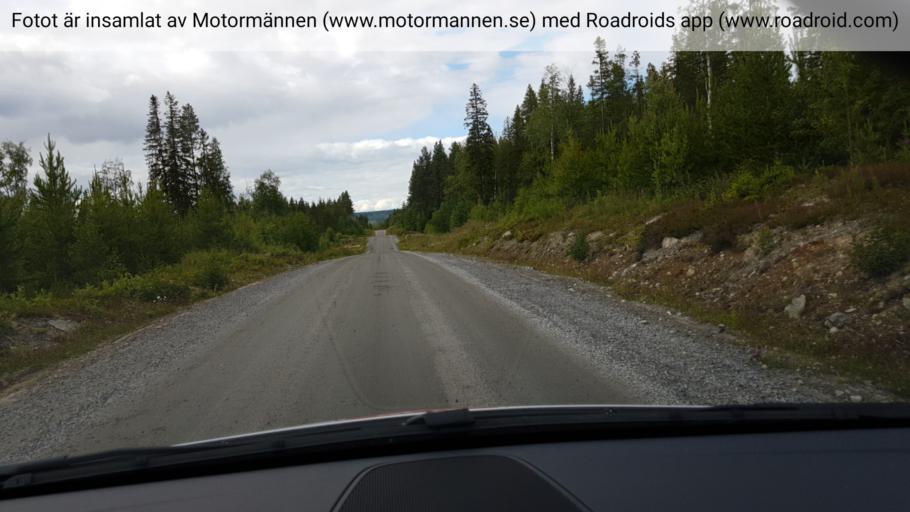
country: SE
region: Vaesterbotten
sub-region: Dorotea Kommun
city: Dorotea
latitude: 63.9360
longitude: 16.0955
